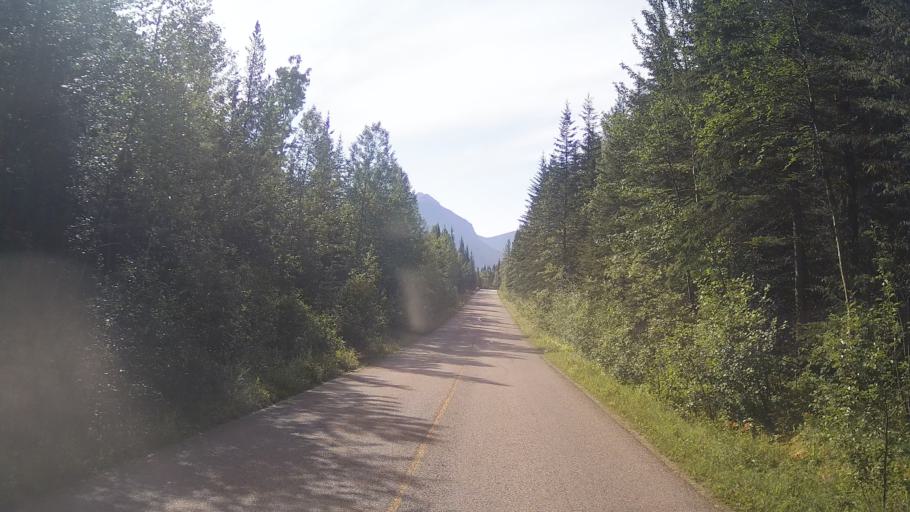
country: CA
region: Alberta
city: Hinton
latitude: 53.1764
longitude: -117.8316
